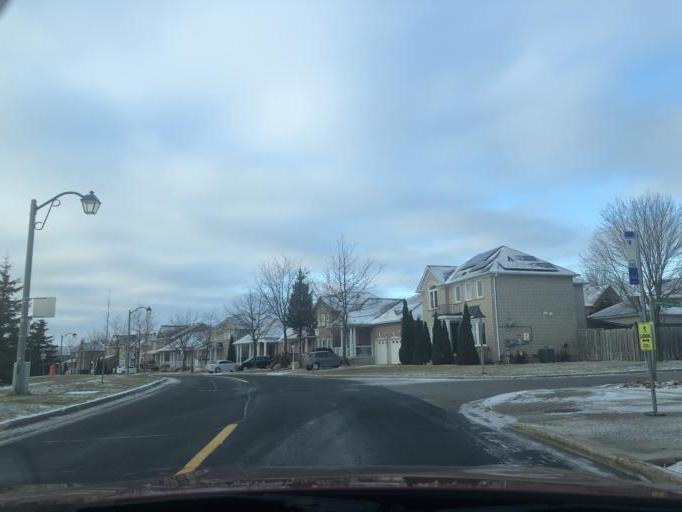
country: CA
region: Ontario
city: Markham
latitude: 43.8648
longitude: -79.2328
